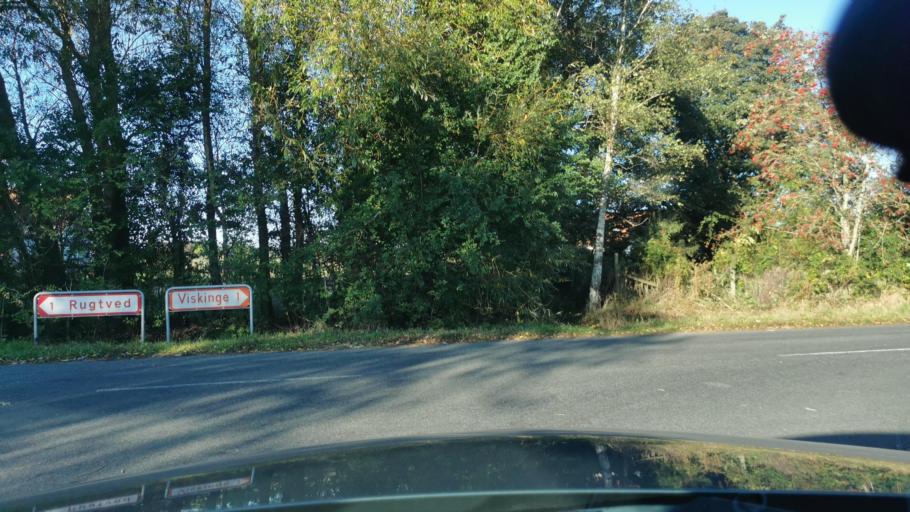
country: DK
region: Zealand
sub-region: Kalundborg Kommune
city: Svebolle
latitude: 55.6539
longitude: 11.2744
